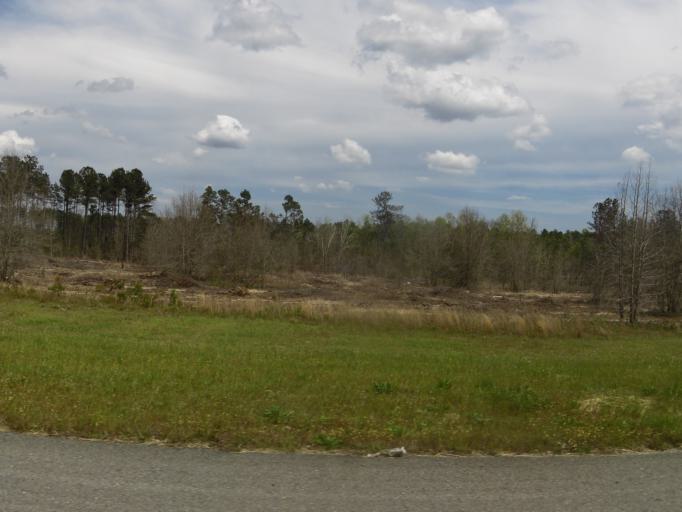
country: US
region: Georgia
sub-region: Jefferson County
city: Wadley
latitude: 32.7331
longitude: -82.3947
